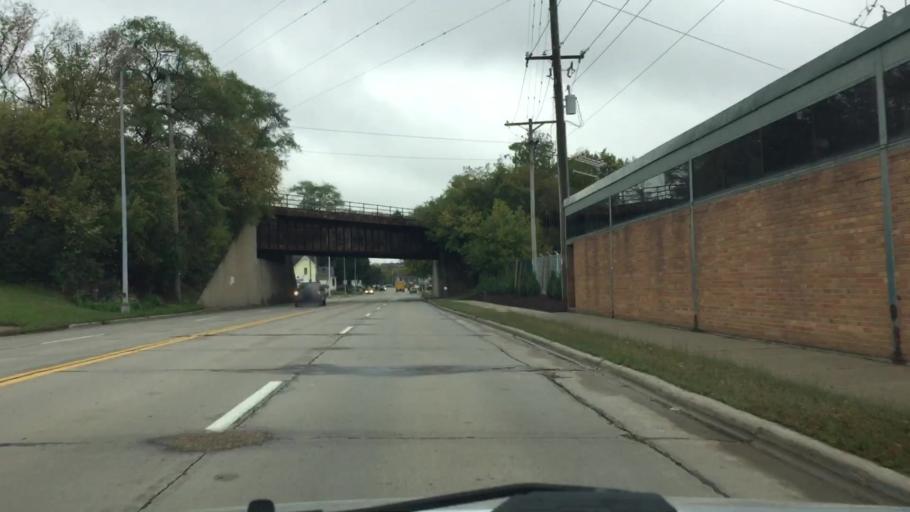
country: US
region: Wisconsin
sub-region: Rock County
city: Janesville
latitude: 42.6896
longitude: -89.0273
